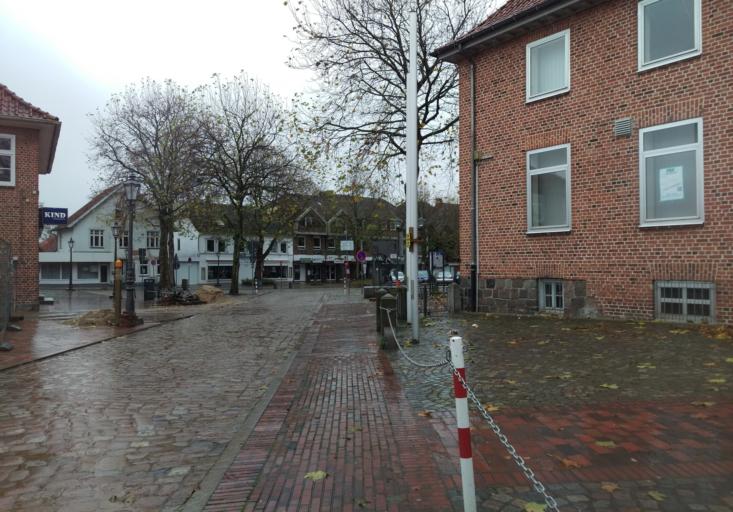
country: DE
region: Schleswig-Holstein
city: Oldenburg in Holstein
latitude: 54.2927
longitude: 10.8863
